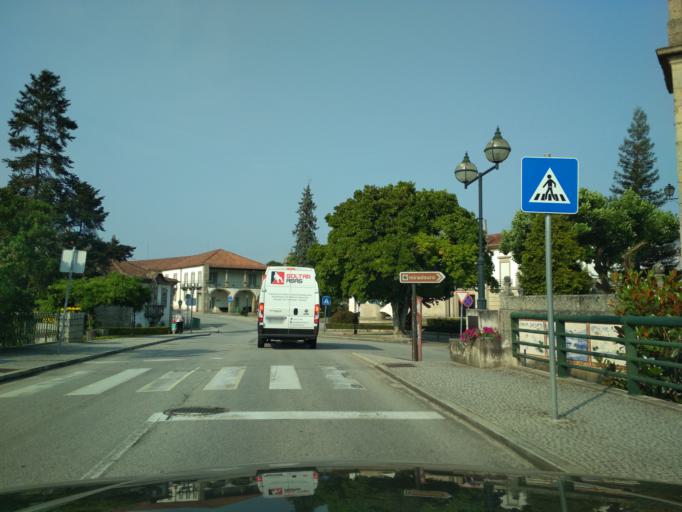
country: PT
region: Viseu
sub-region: Santa Comba Dao
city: Santa Comba Dao
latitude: 40.3954
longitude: -8.1312
